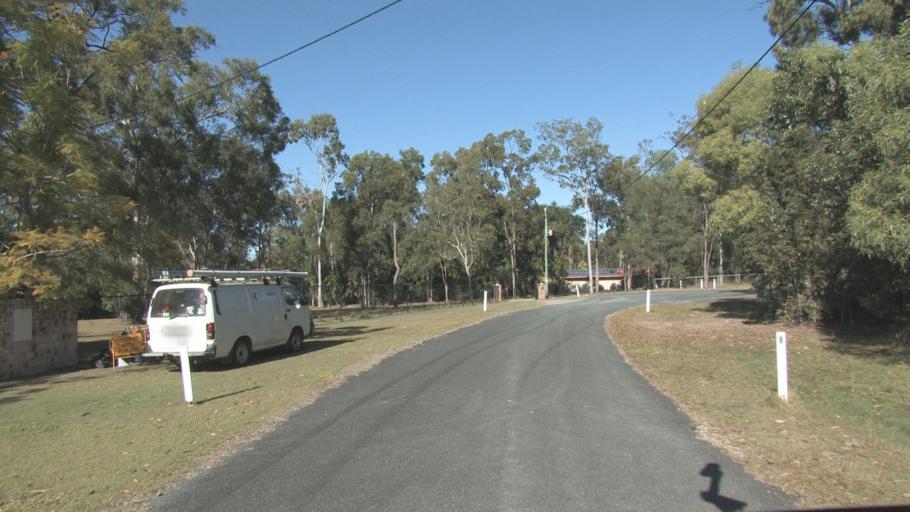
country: AU
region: Queensland
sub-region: Logan
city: Chambers Flat
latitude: -27.7510
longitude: 153.0509
